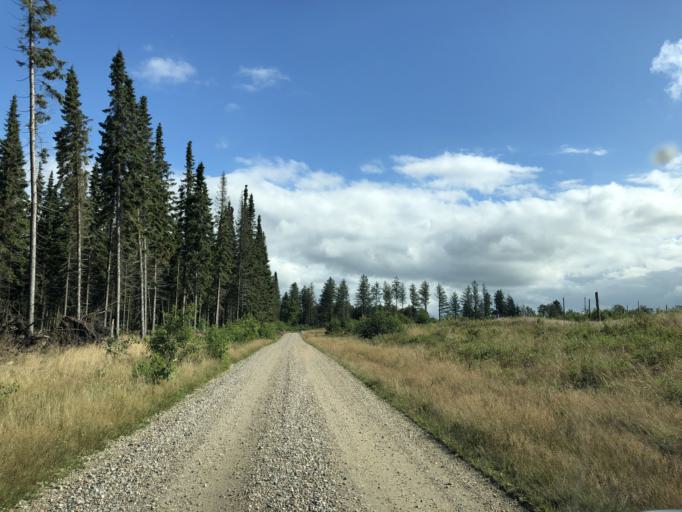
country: DK
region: Central Jutland
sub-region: Holstebro Kommune
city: Ulfborg
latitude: 56.2468
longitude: 8.4869
